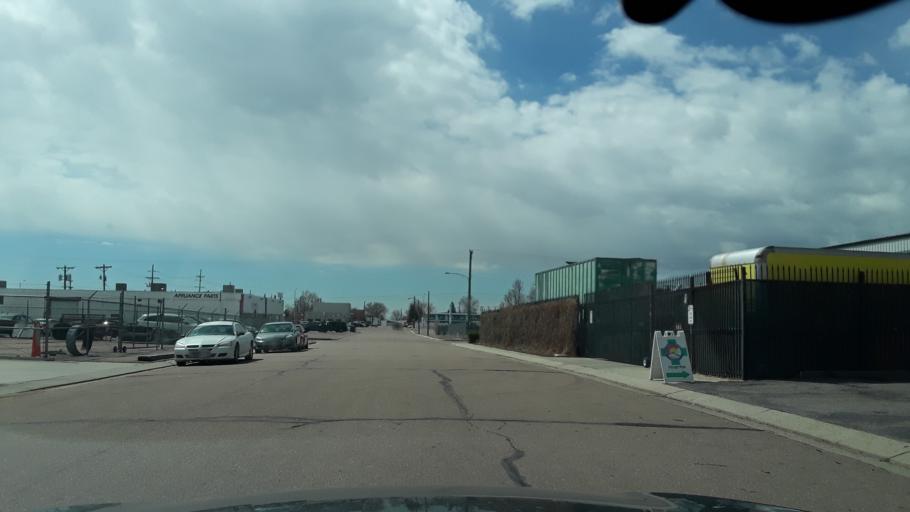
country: US
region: Colorado
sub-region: El Paso County
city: Colorado Springs
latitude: 38.8417
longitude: -104.7720
